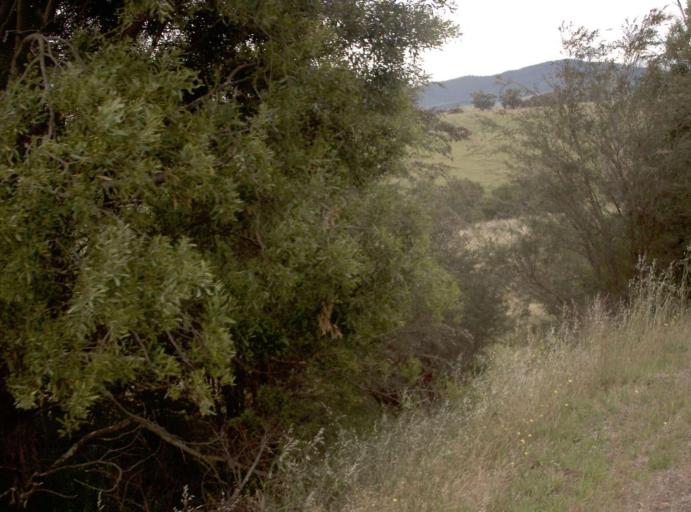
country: AU
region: Victoria
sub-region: East Gippsland
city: Bairnsdale
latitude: -37.4719
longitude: 147.2331
